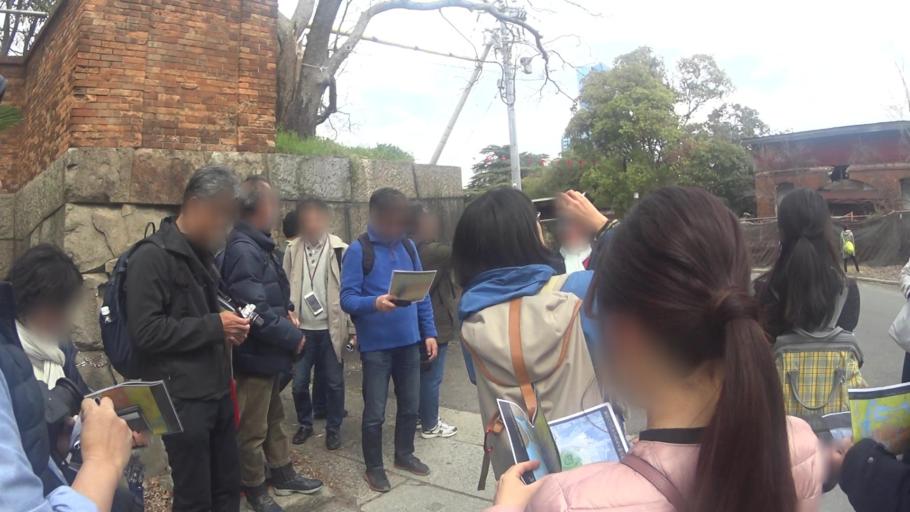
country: JP
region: Osaka
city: Osaka-shi
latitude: 34.6903
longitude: 135.5227
